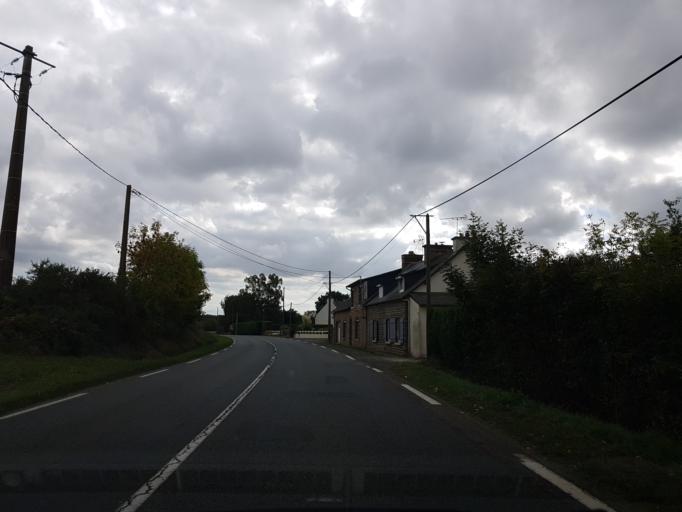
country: FR
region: Brittany
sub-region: Departement des Cotes-d'Armor
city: Pommeret
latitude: 48.4537
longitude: -2.6483
